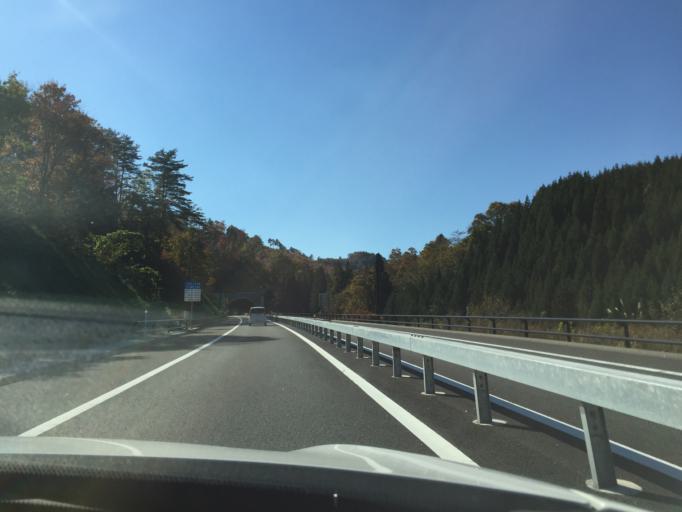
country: JP
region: Miyagi
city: Marumori
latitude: 37.7865
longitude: 140.7588
